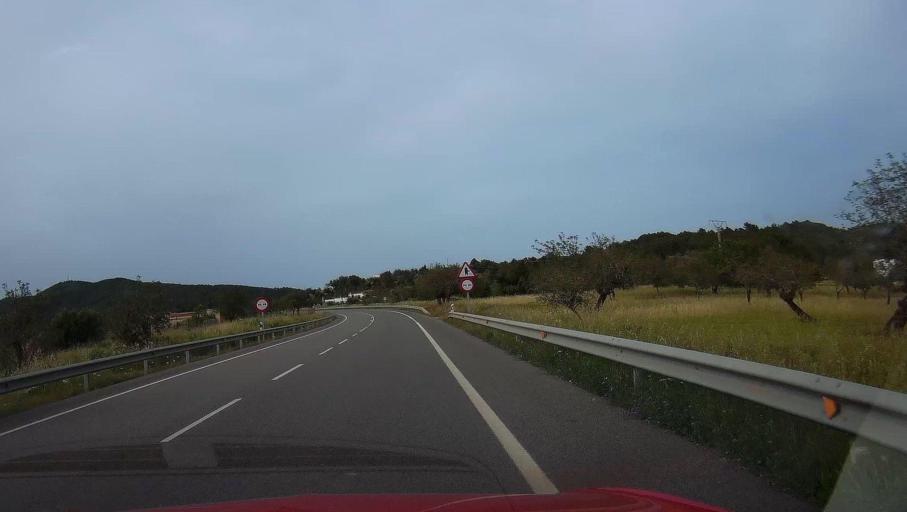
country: ES
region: Balearic Islands
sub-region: Illes Balears
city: Sant Joan de Labritja
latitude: 39.0609
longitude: 1.4945
